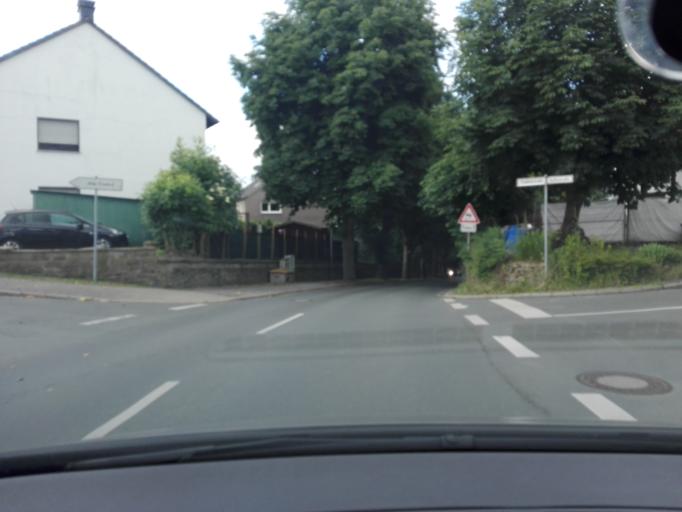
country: DE
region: North Rhine-Westphalia
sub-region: Regierungsbezirk Arnsberg
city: Frondenberg
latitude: 51.4770
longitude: 7.7689
